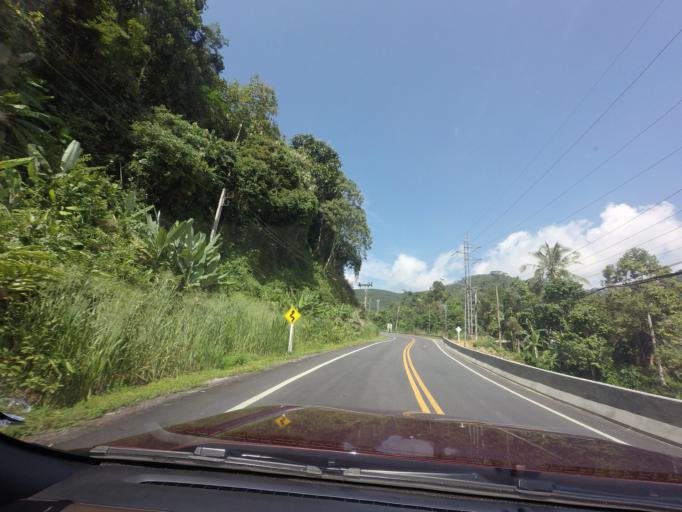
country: TH
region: Yala
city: Betong
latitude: 5.9034
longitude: 101.1476
